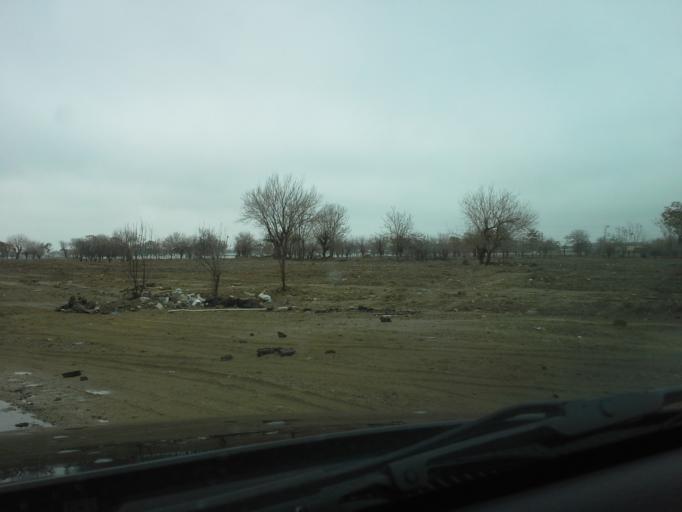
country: TM
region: Ahal
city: Ashgabat
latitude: 37.9558
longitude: 58.4238
